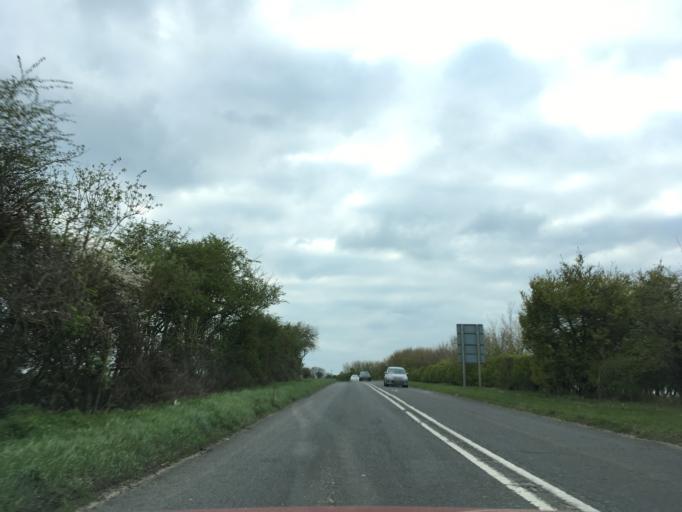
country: GB
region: England
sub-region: Oxfordshire
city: Carterton
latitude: 51.7892
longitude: -1.5725
